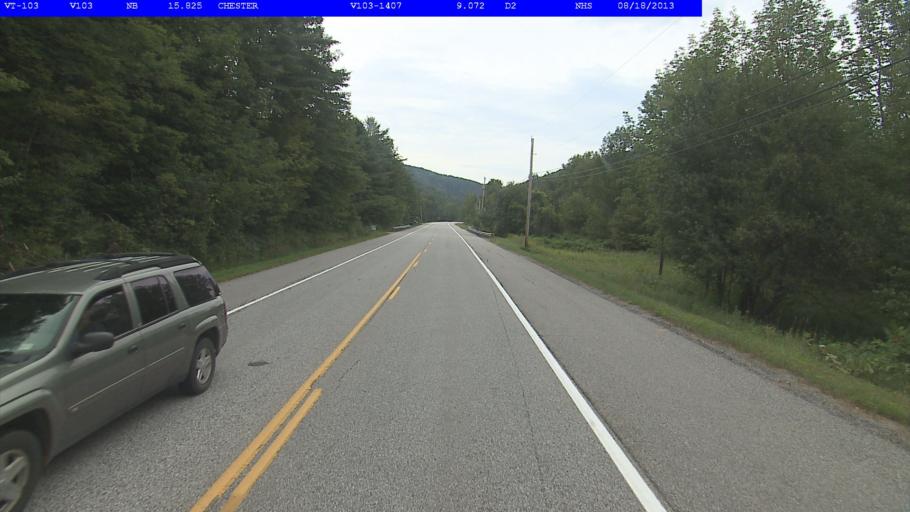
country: US
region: Vermont
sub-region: Windsor County
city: Chester
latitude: 43.3410
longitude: -72.6197
